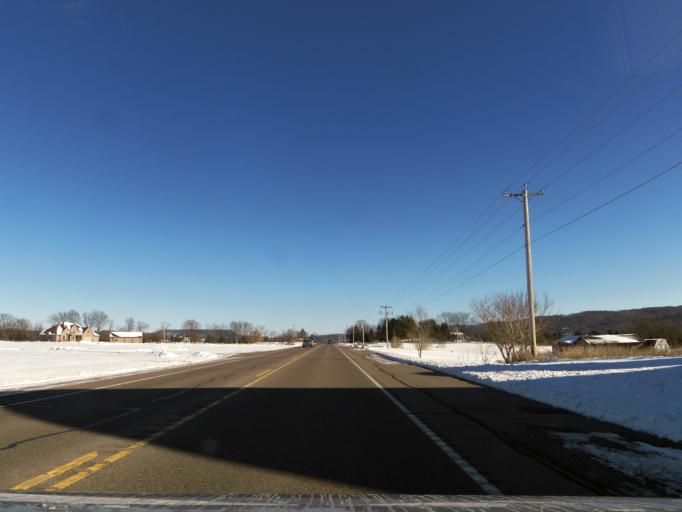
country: US
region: Wisconsin
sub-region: Sauk County
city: Baraboo
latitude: 43.4743
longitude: -89.6691
